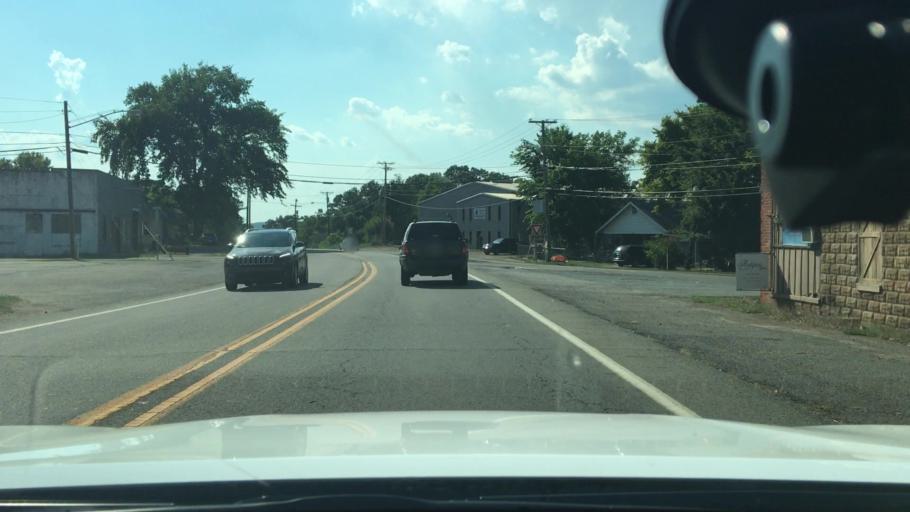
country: US
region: Arkansas
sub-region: Johnson County
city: Clarksville
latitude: 35.4722
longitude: -93.4823
